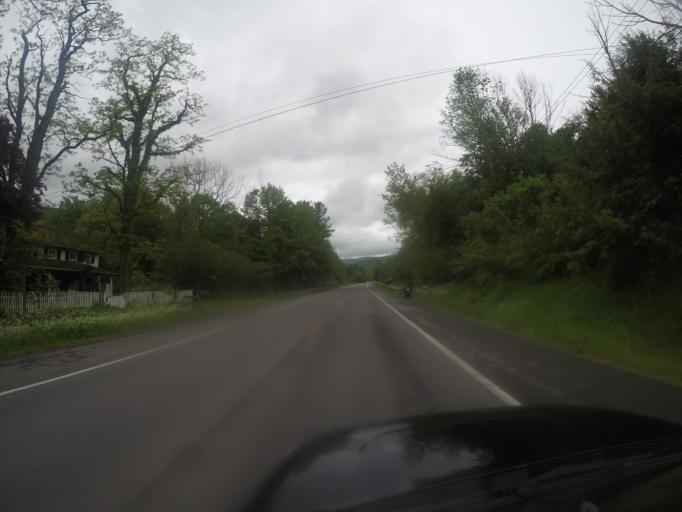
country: US
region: New York
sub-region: Ulster County
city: Shokan
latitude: 42.1016
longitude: -74.3461
